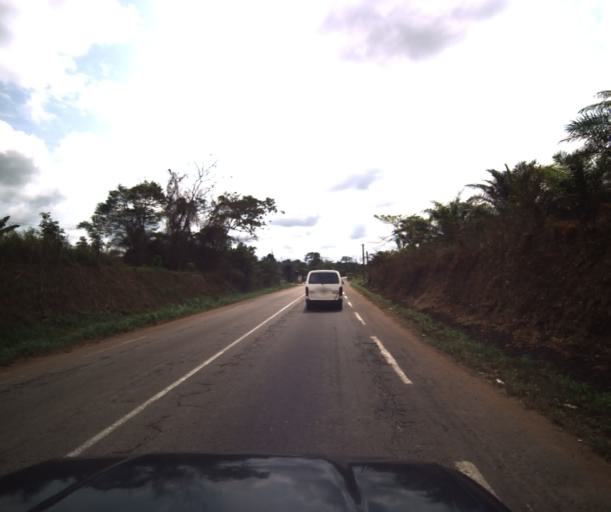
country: CM
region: Centre
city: Eseka
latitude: 3.8579
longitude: 10.5591
